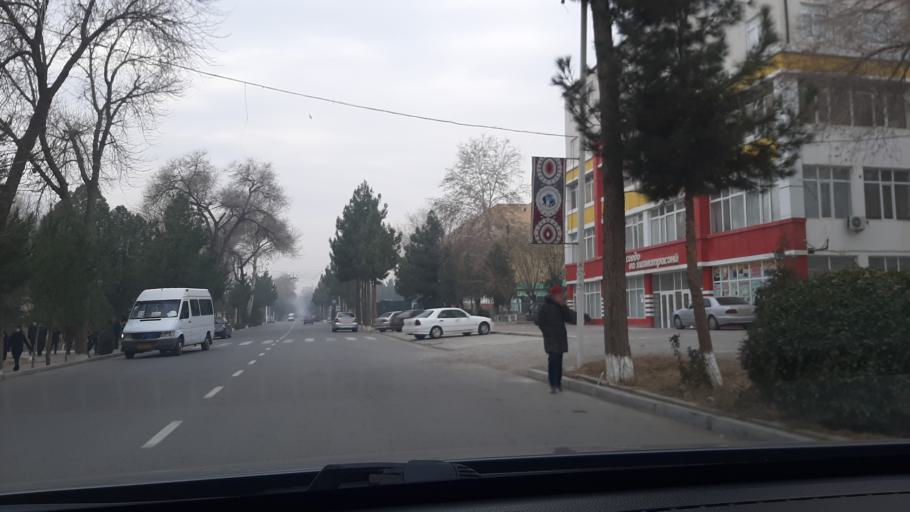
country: TJ
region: Viloyati Sughd
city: Palos
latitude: 40.2651
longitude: 69.7958
